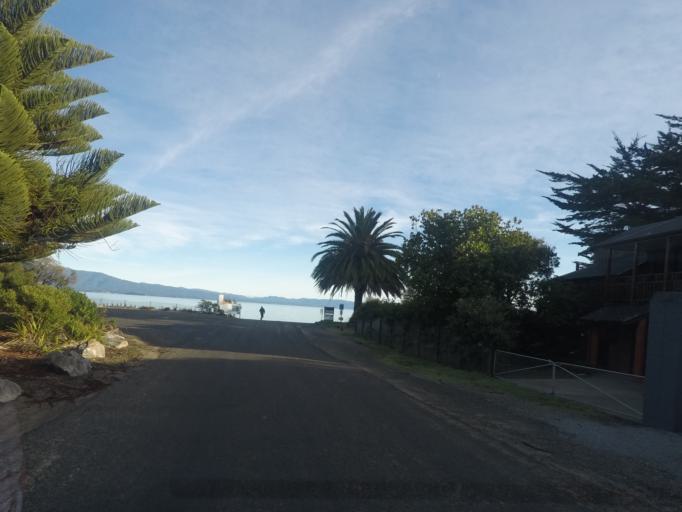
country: NZ
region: Tasman
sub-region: Tasman District
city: Takaka
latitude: -40.8118
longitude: 172.9155
